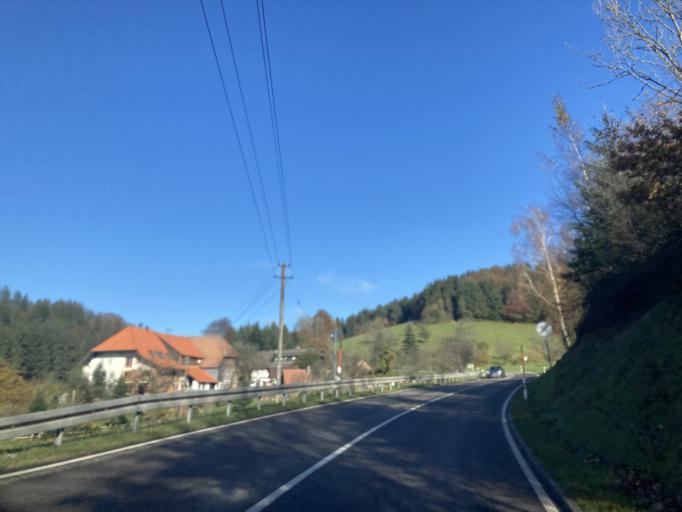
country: DE
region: Baden-Wuerttemberg
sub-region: Freiburg Region
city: Elzach
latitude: 48.2063
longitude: 8.0877
